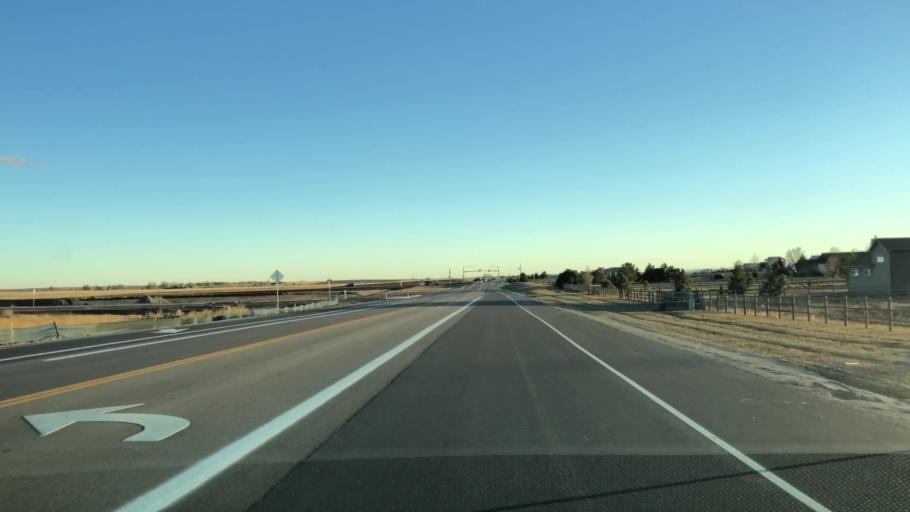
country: US
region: Colorado
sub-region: Weld County
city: Windsor
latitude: 40.4402
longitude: -104.9443
